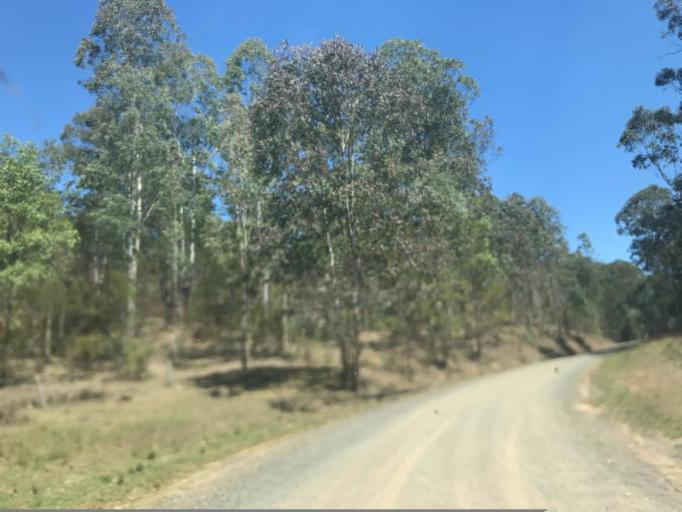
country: AU
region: New South Wales
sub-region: Hornsby Shire
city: Glenorie
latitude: -33.2579
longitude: 150.9757
